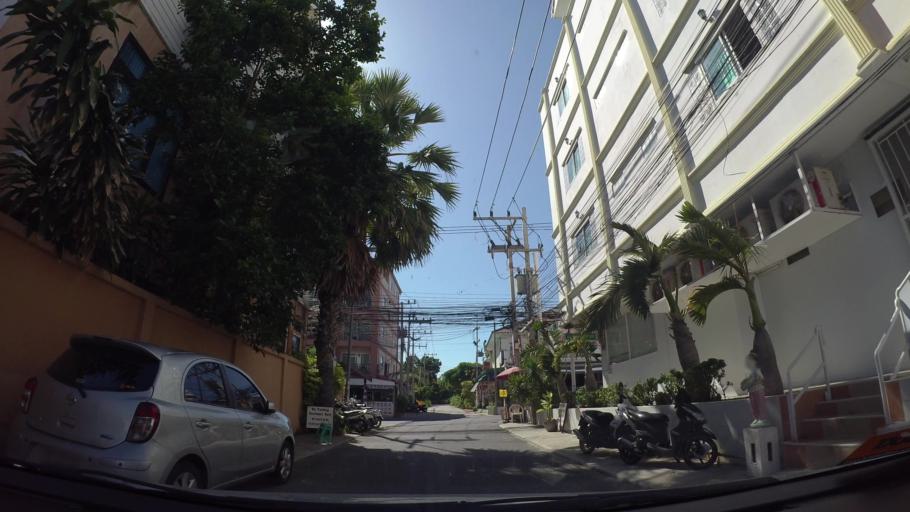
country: TH
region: Chon Buri
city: Phatthaya
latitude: 12.9107
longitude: 100.8602
